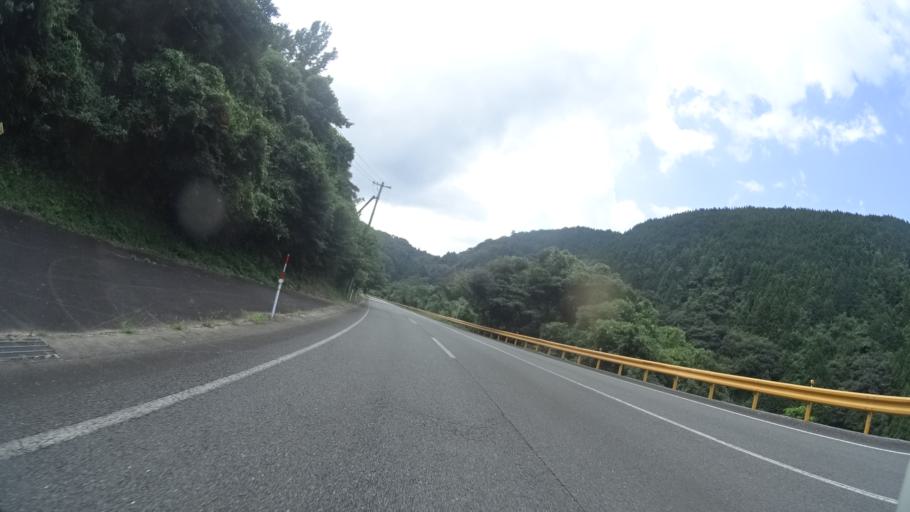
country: JP
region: Shimane
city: Masuda
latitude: 34.5887
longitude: 131.6109
